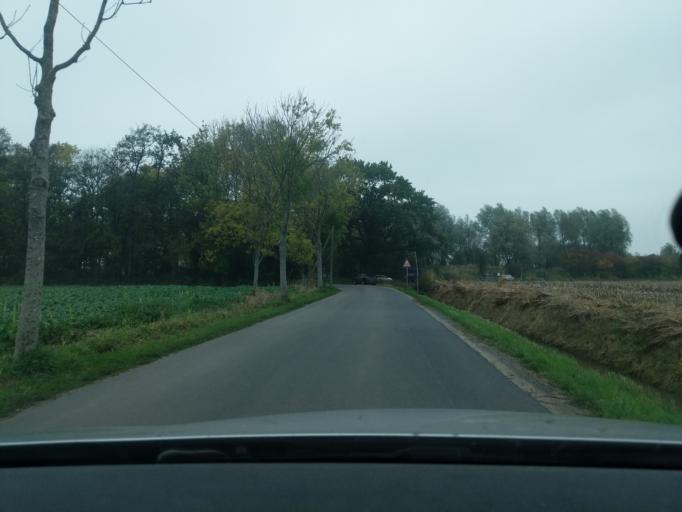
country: DE
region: Lower Saxony
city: Otterndorf
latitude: 53.8207
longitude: 8.8663
